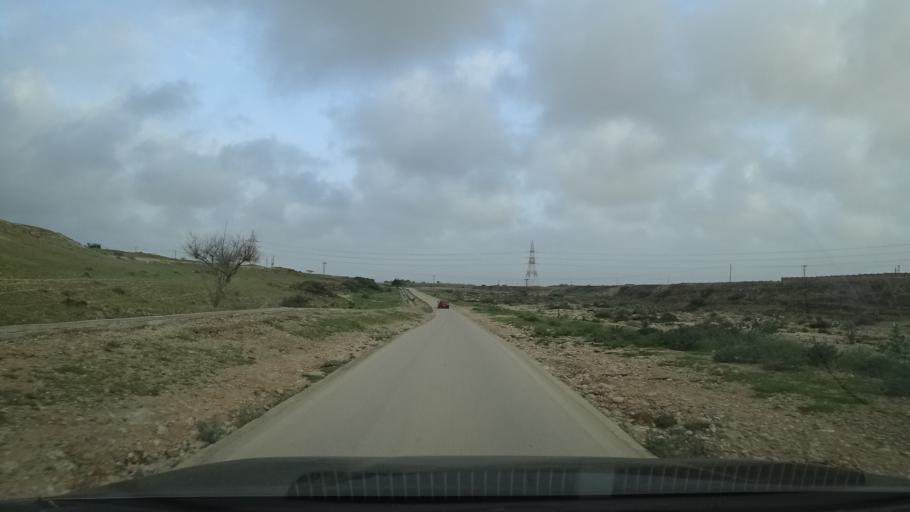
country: OM
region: Zufar
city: Salalah
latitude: 17.1078
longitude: 54.2293
